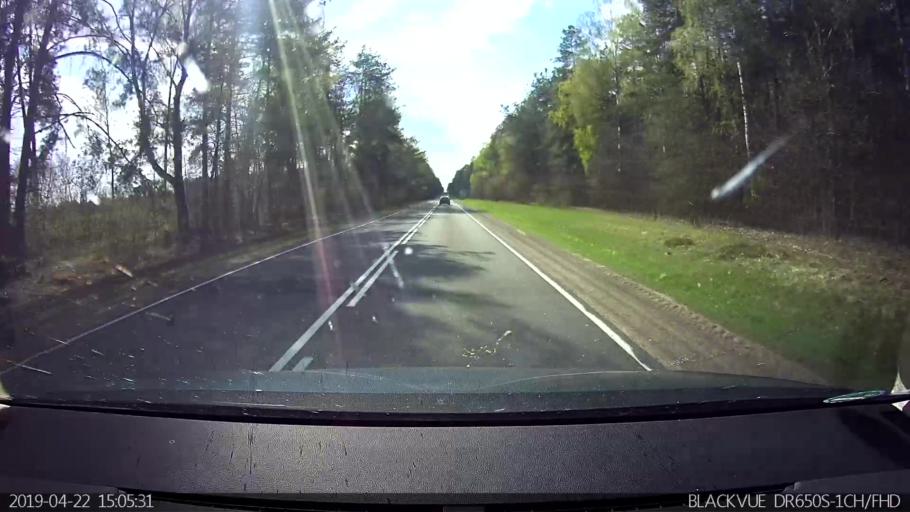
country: BY
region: Brest
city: Kamyanyets
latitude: 52.3341
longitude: 23.8645
